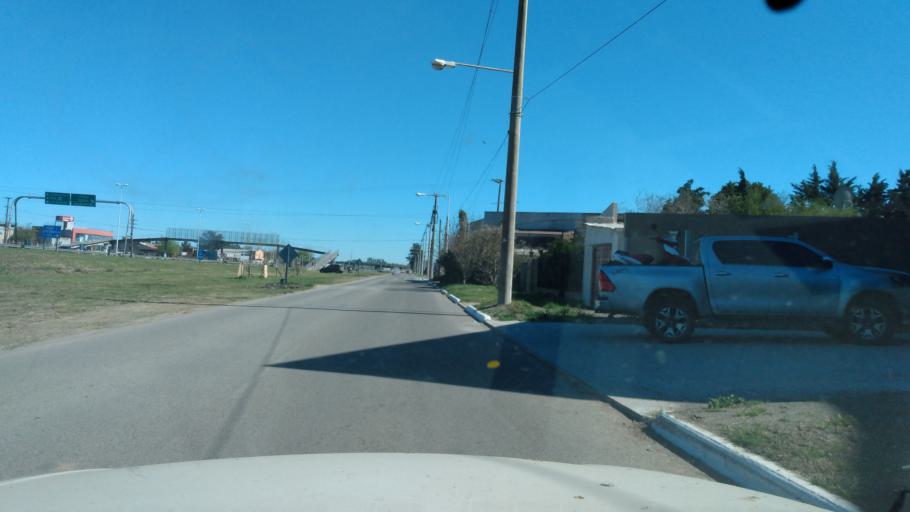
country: AR
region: Buenos Aires
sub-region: Partido de Lujan
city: Lujan
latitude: -34.5546
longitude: -59.1020
